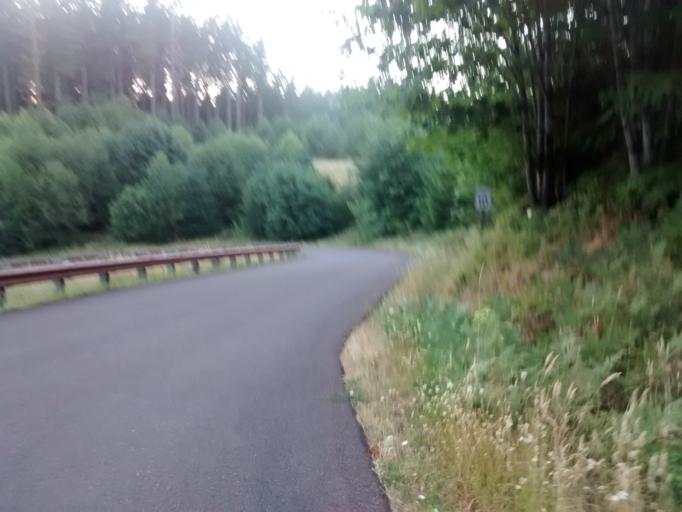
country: US
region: Oregon
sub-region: Columbia County
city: Vernonia
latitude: 45.7444
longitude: -123.1837
